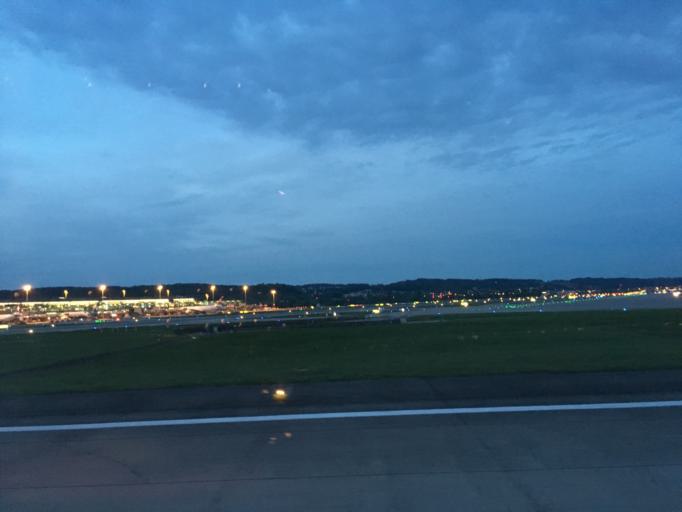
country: CH
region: Zurich
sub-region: Bezirk Dielsdorf
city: Ruemlang / Ruemlang (Dorfkern)
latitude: 47.4565
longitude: 8.5493
